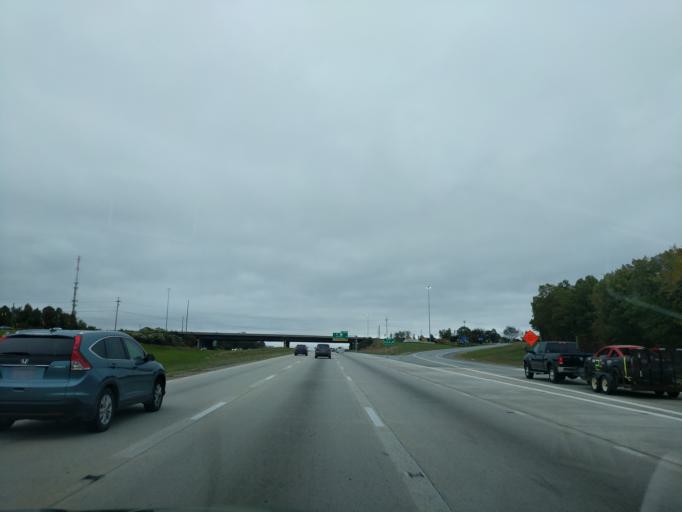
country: US
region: North Carolina
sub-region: Randolph County
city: Archdale
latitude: 35.9204
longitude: -79.9393
